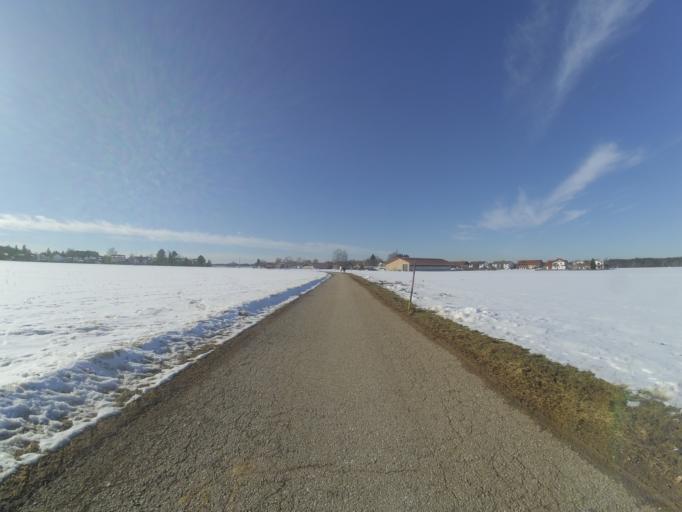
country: DE
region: Bavaria
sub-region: Upper Bavaria
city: Hohenkirchen-Siegertsbrunn
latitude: 47.9907
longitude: 11.7417
